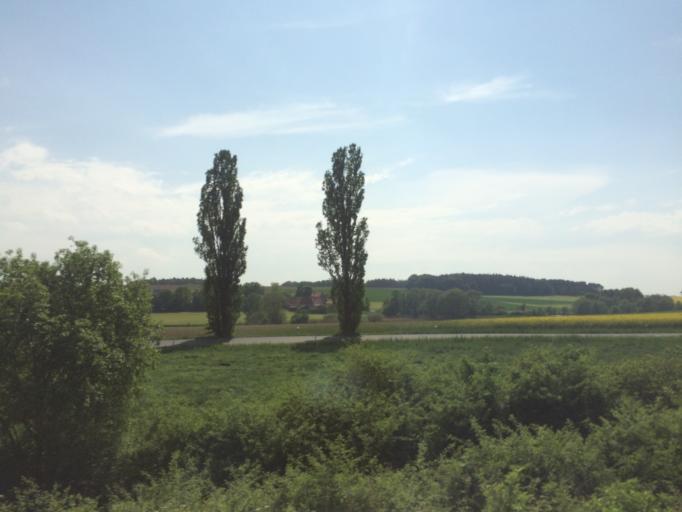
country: DE
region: Bavaria
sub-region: Regierungsbezirk Mittelfranken
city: Emskirchen
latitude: 49.5568
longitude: 10.6982
